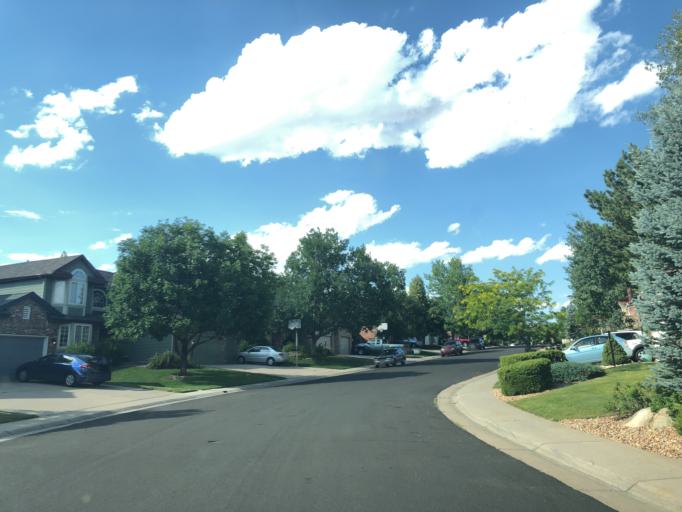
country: US
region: Colorado
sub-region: Arapahoe County
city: Dove Valley
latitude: 39.6081
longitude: -104.7633
